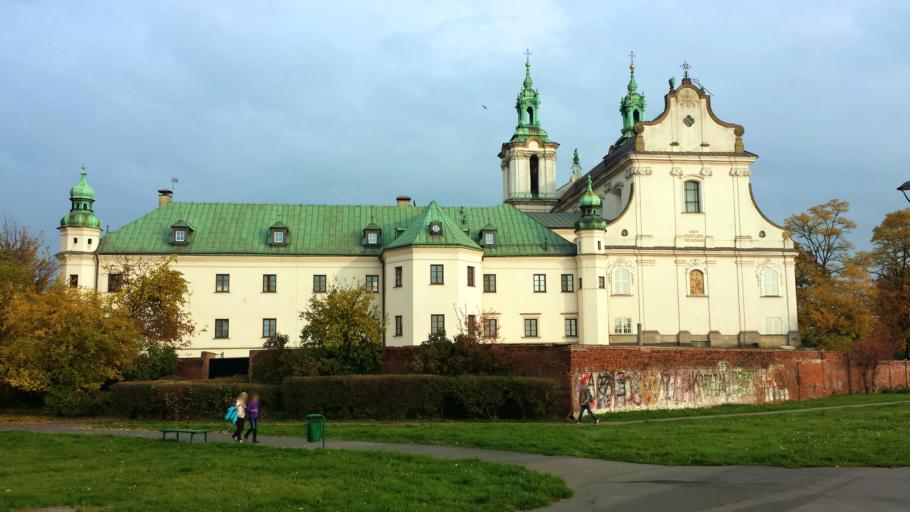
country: PL
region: Lesser Poland Voivodeship
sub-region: Krakow
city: Krakow
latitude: 50.0488
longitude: 19.9365
